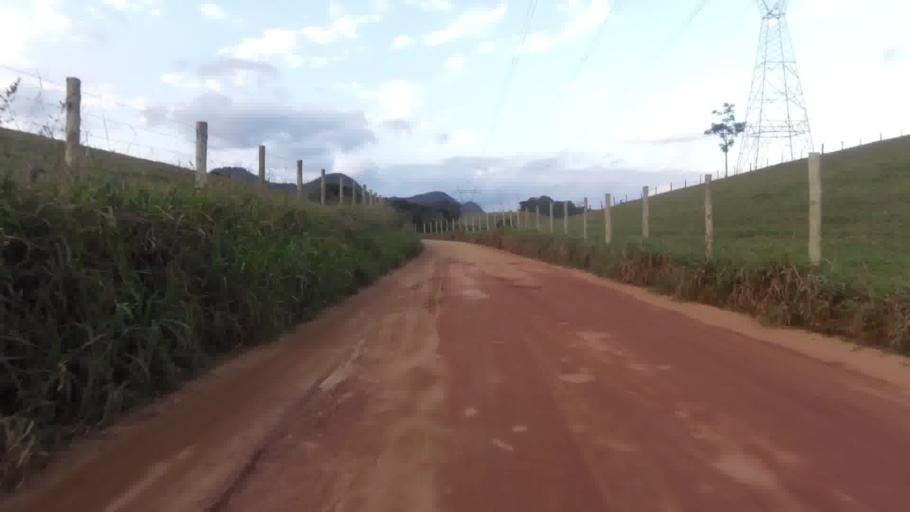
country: BR
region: Espirito Santo
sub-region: Guarapari
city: Guarapari
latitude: -20.6749
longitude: -40.6155
